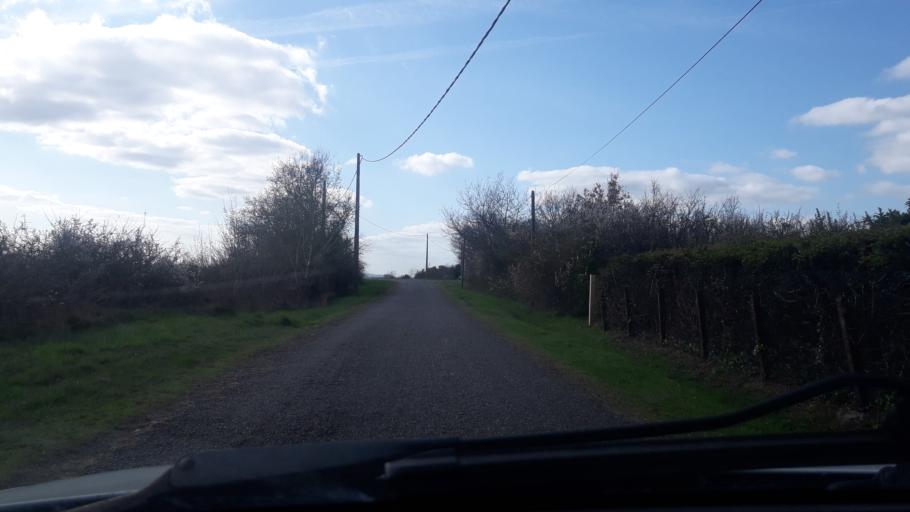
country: FR
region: Midi-Pyrenees
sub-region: Departement de la Haute-Garonne
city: Montesquieu-Volvestre
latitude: 43.2134
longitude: 1.2329
